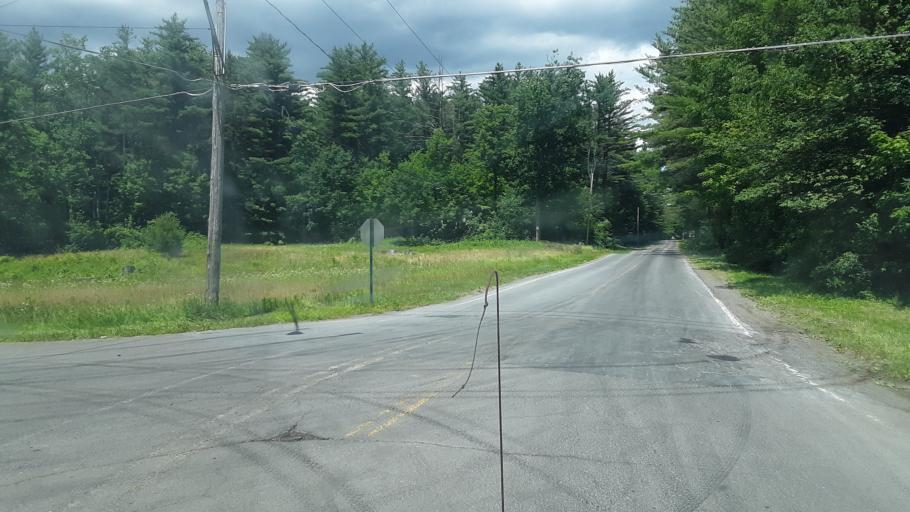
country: US
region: New York
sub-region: Oneida County
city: Rome
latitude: 43.2519
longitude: -75.5966
